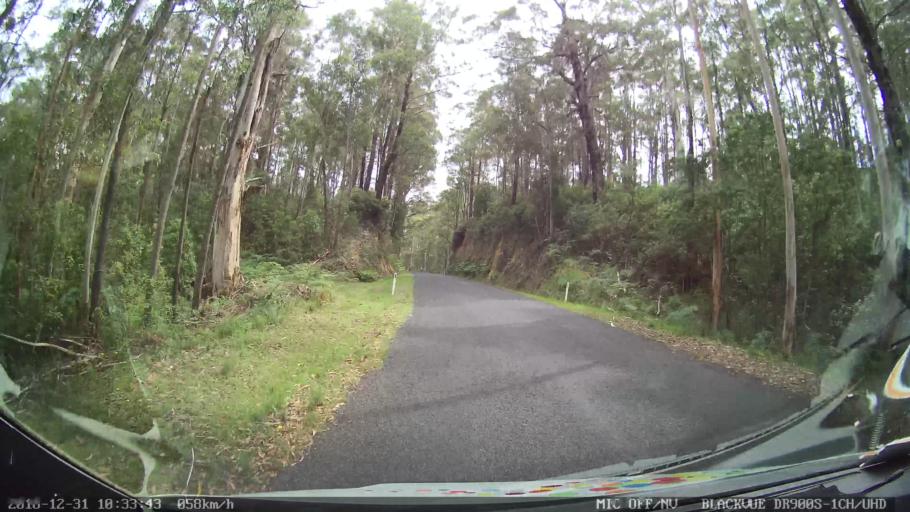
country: AU
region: New South Wales
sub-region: Snowy River
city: Jindabyne
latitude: -36.4455
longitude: 148.1664
